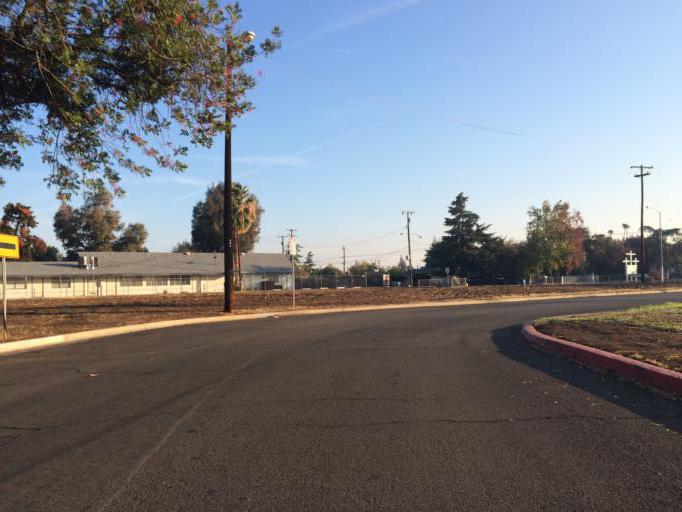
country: US
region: California
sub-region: Fresno County
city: Fresno
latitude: 36.7921
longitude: -119.7641
